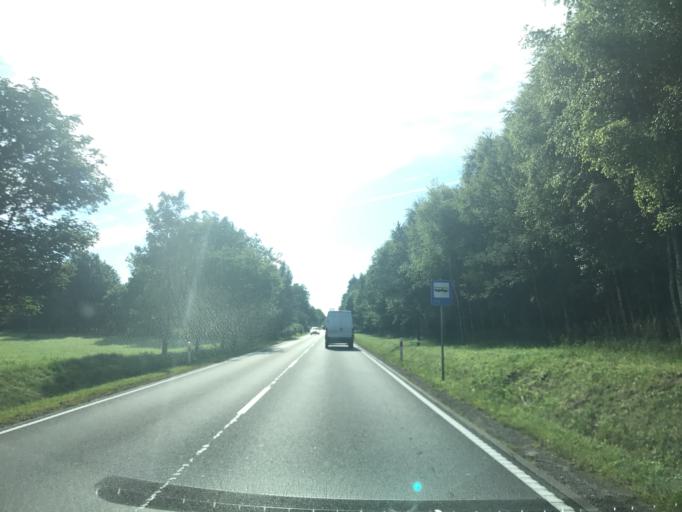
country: PL
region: Pomeranian Voivodeship
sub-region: Powiat czluchowski
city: Rzeczenica
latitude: 53.7510
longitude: 17.1476
